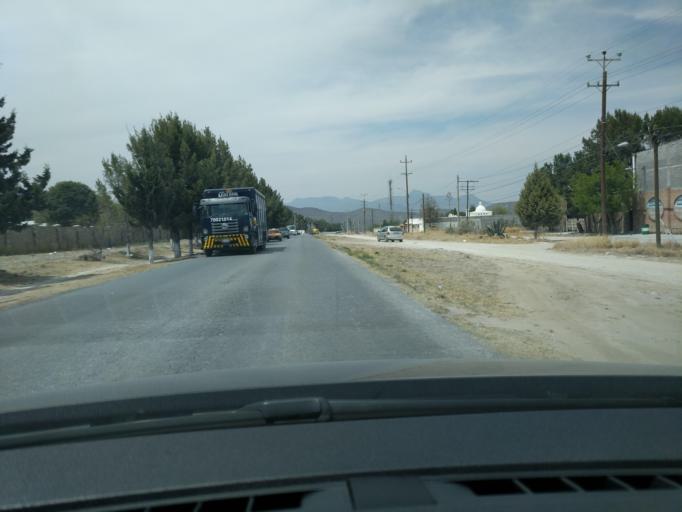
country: MX
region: Coahuila
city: Saltillo
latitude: 25.3552
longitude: -101.0291
